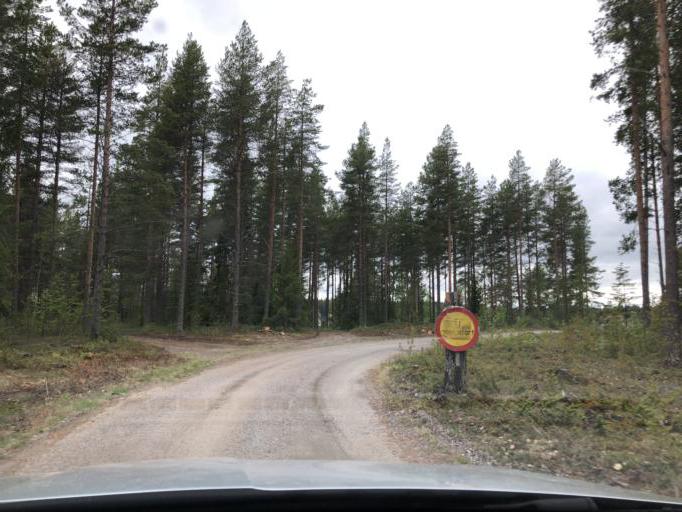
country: SE
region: Norrbotten
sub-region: Pitea Kommun
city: Pitea
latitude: 65.2407
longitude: 21.5214
